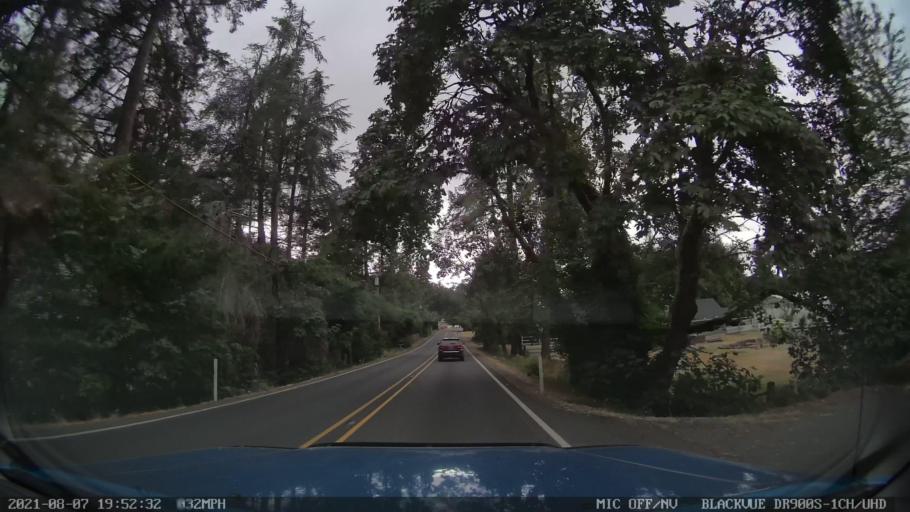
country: US
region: Oregon
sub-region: Marion County
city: Silverton
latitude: 44.9846
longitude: -122.7589
